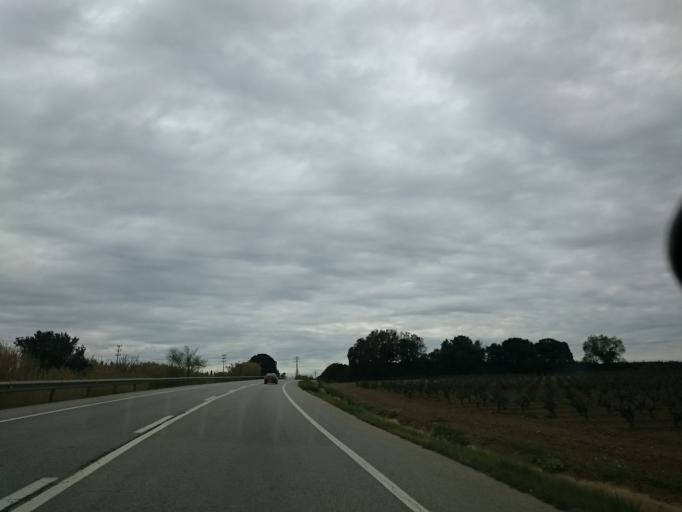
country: ES
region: Catalonia
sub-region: Provincia de Barcelona
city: La Granada
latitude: 41.3875
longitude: 1.7409
